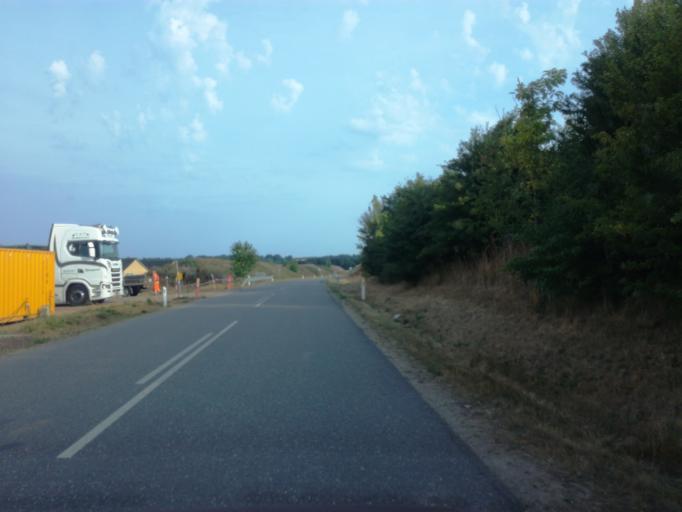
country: DK
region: South Denmark
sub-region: Vejle Kommune
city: Borkop
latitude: 55.6406
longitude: 9.6375
